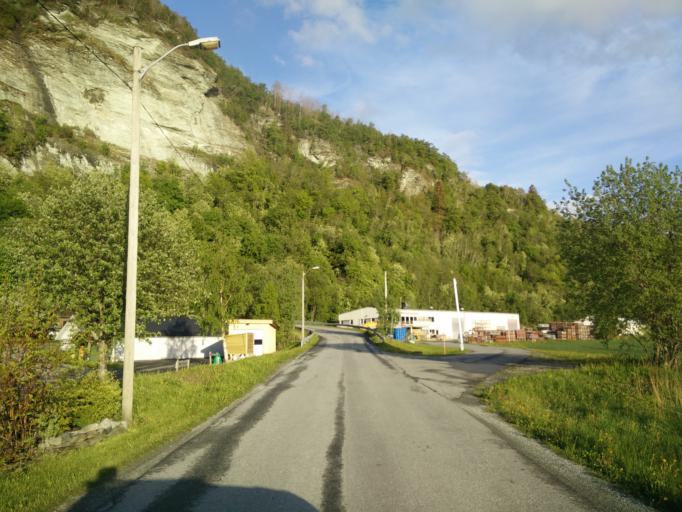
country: NO
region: Sor-Trondelag
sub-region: Melhus
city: Melhus
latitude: 63.3146
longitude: 10.1956
